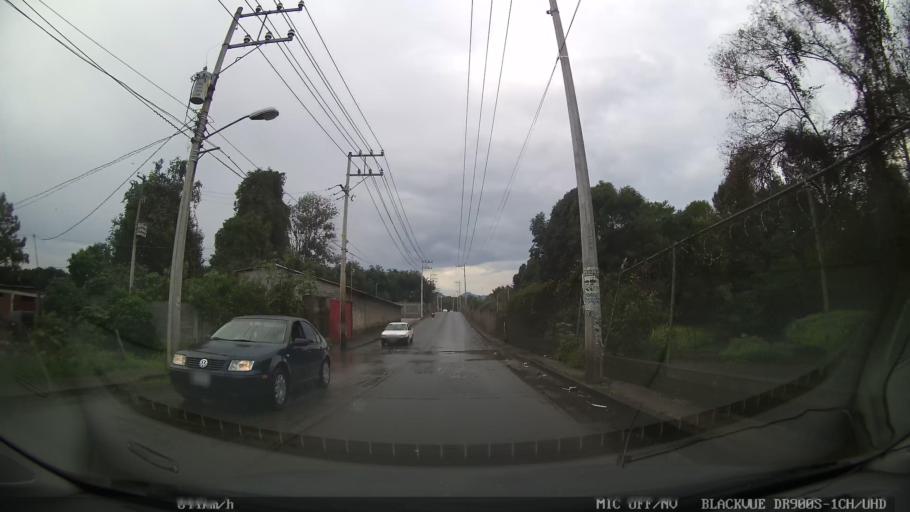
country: MX
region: Michoacan
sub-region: Uruapan
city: Santa Rosa (Santa Barbara)
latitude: 19.3837
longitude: -102.0477
